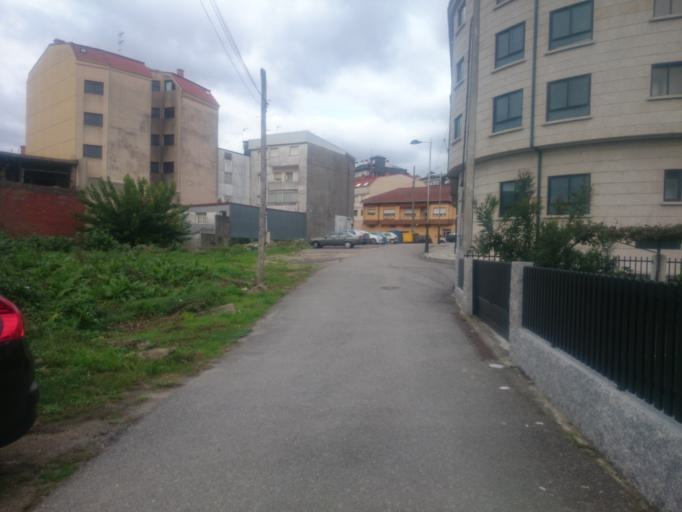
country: ES
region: Galicia
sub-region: Provincia de Pontevedra
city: Porrino
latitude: 42.1557
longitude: -8.6218
